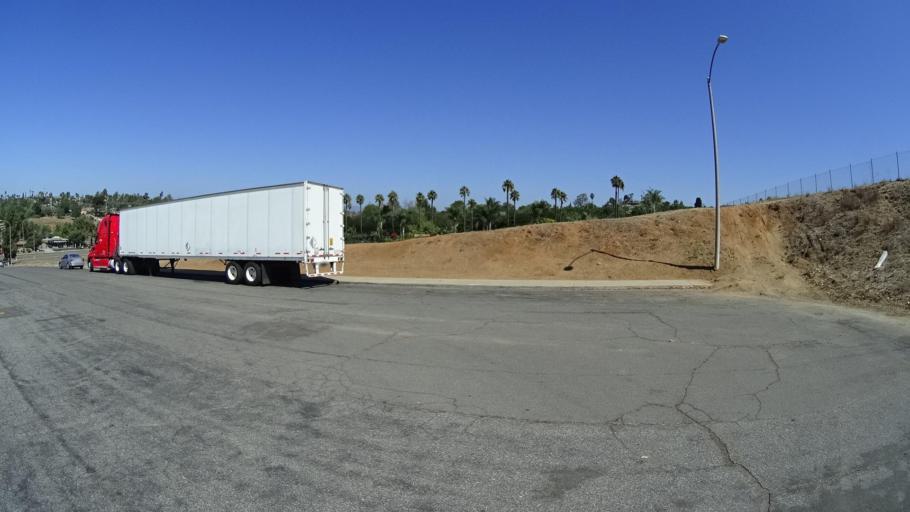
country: US
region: California
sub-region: San Diego County
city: Fallbrook
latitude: 33.3625
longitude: -117.2473
